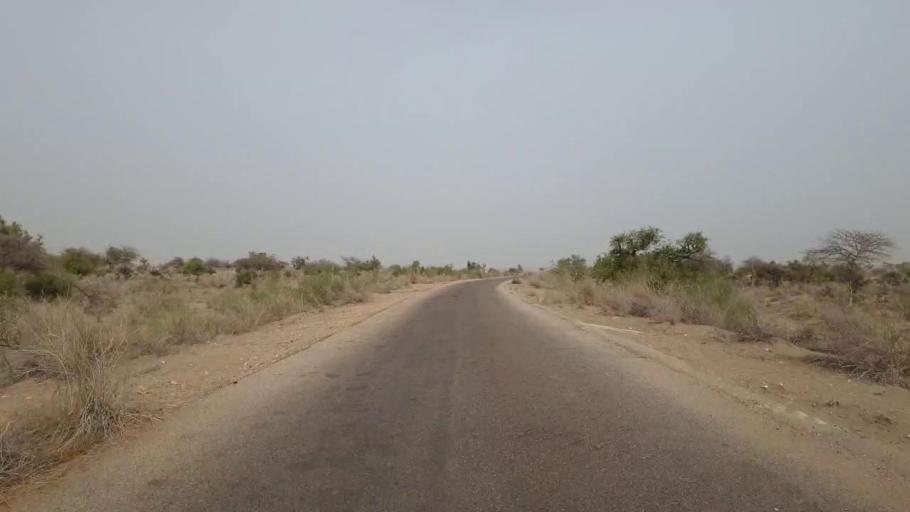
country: PK
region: Sindh
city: Islamkot
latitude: 24.5583
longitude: 70.3448
